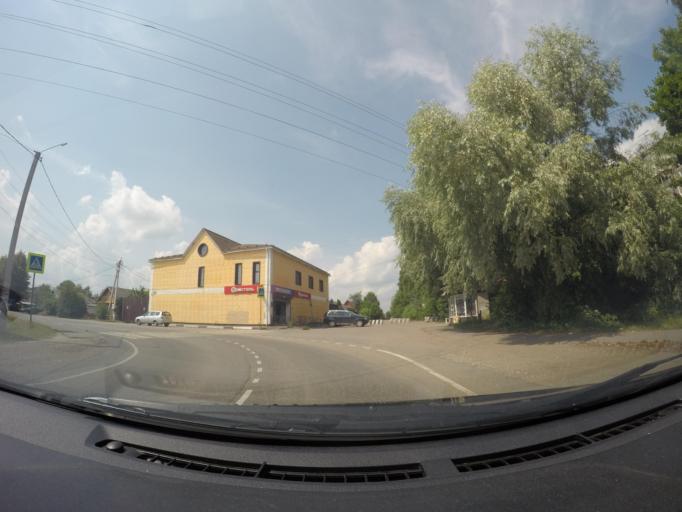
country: RU
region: Moskovskaya
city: Bronnitsy
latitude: 55.4192
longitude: 38.2880
